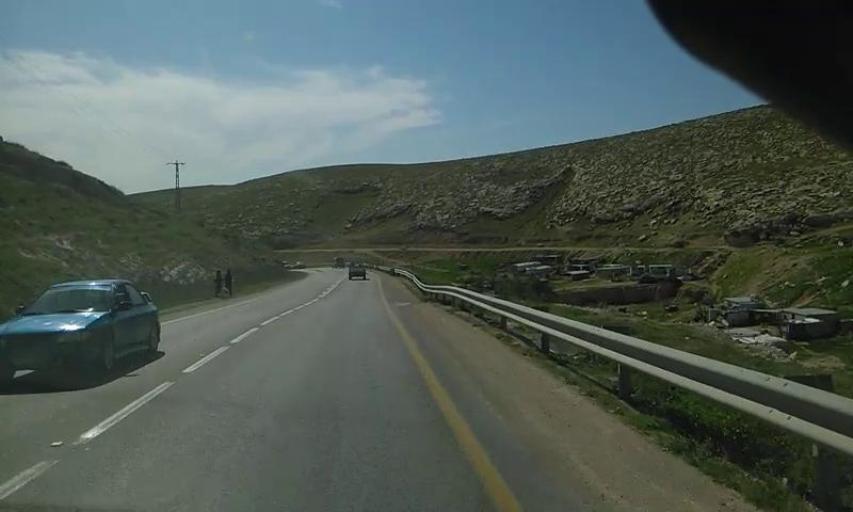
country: PS
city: Az Za`ayyim
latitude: 31.8077
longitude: 35.3079
